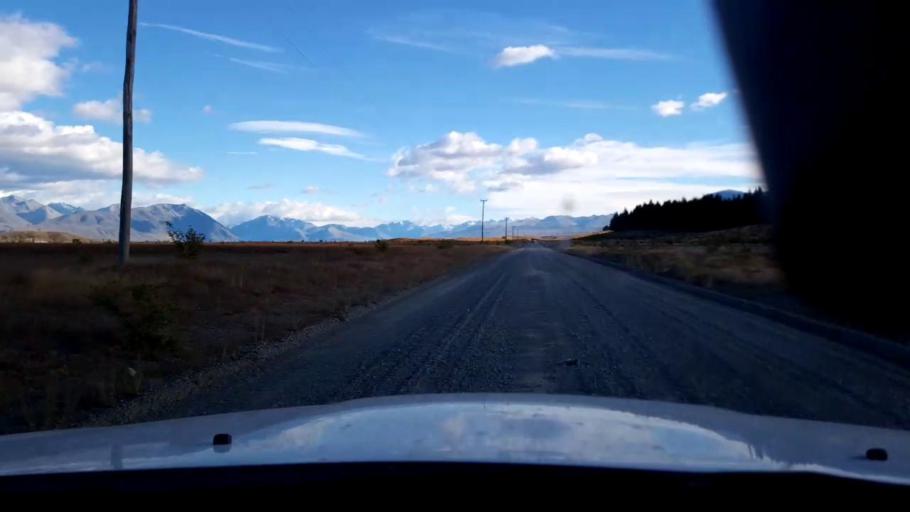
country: NZ
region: Canterbury
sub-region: Timaru District
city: Pleasant Point
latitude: -43.9862
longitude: 170.5054
